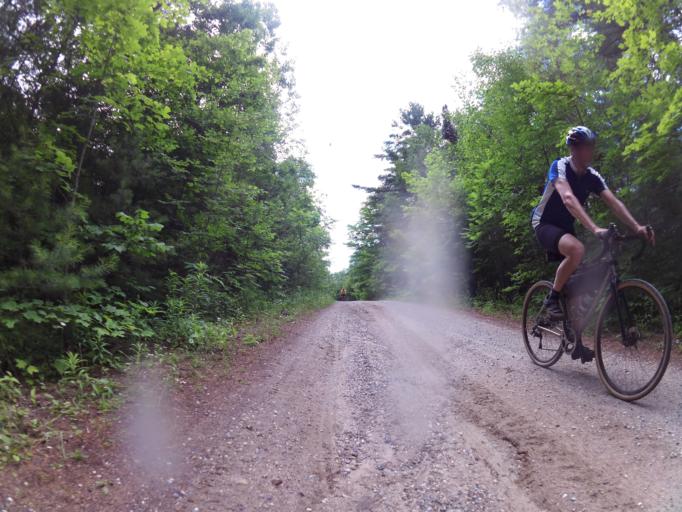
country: CA
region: Ontario
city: Perth
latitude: 45.0150
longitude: -76.5993
